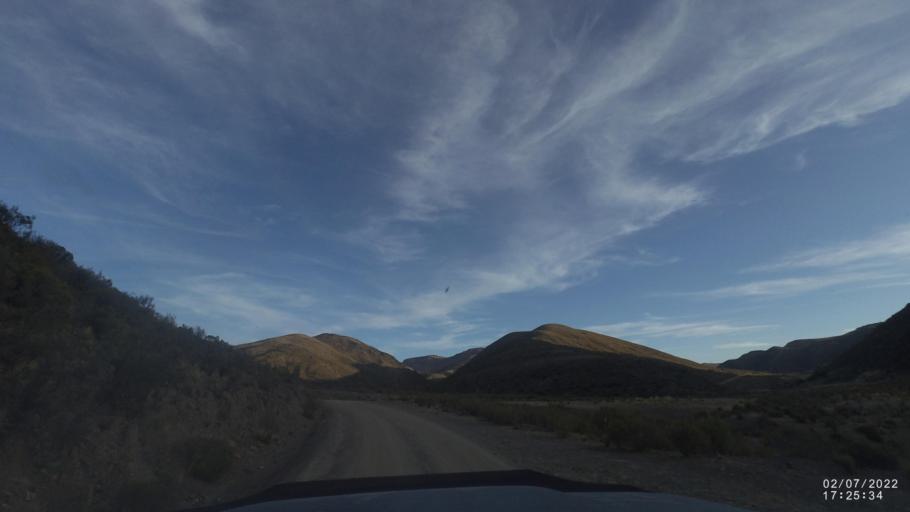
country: BO
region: Cochabamba
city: Irpa Irpa
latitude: -17.8771
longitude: -66.6079
